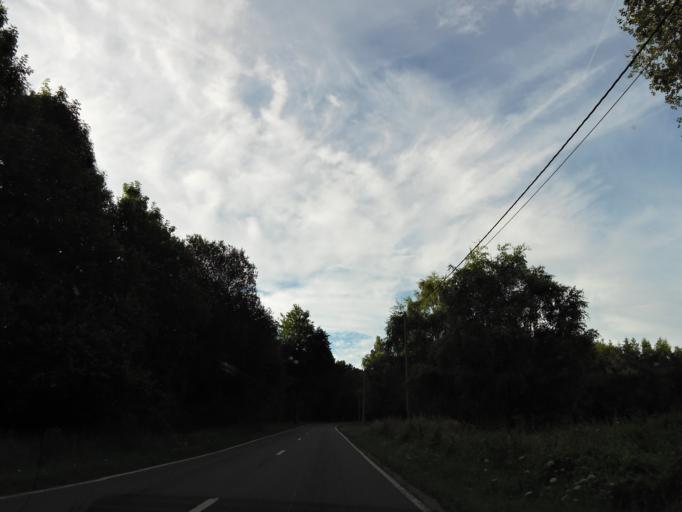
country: BE
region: Wallonia
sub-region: Province de Liege
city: Jalhay
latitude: 50.5059
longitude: 5.9563
